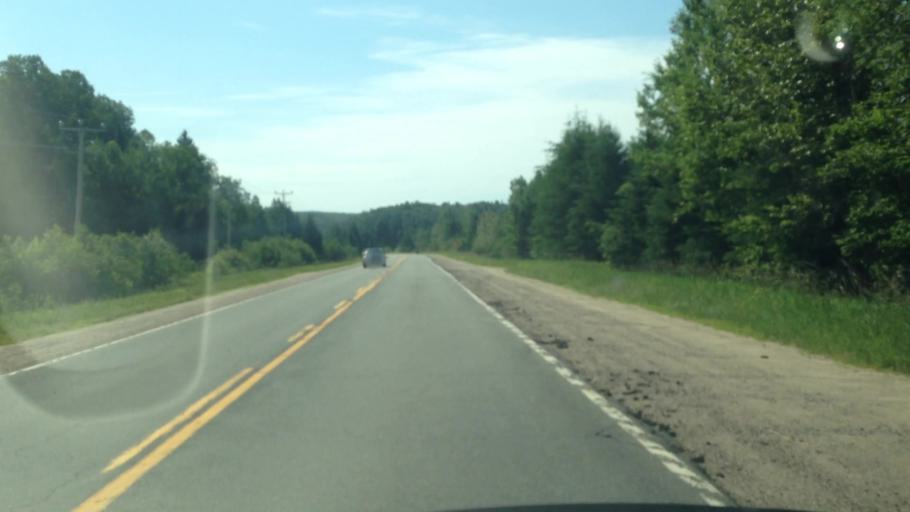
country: CA
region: Quebec
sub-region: Laurentides
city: Mont-Tremblant
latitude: 46.0557
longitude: -74.6173
